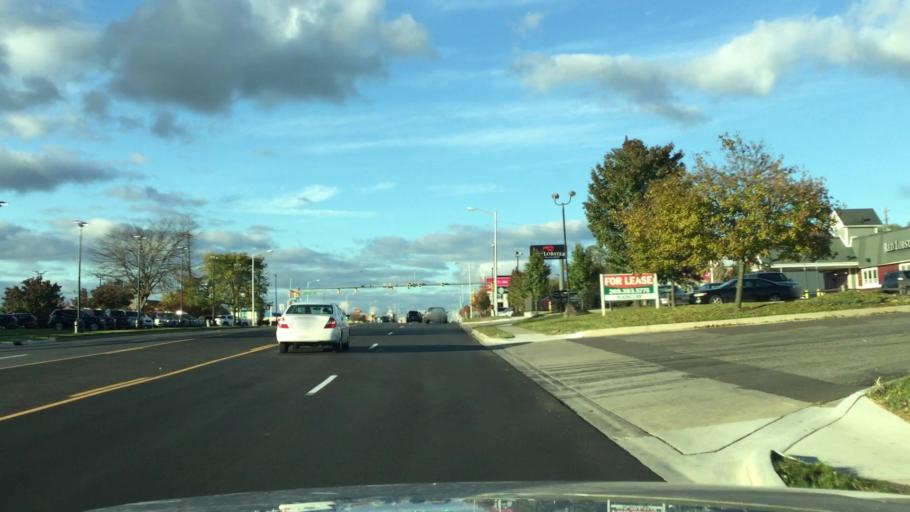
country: US
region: Michigan
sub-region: Kalamazoo County
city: Portage
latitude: 42.2210
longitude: -85.5894
